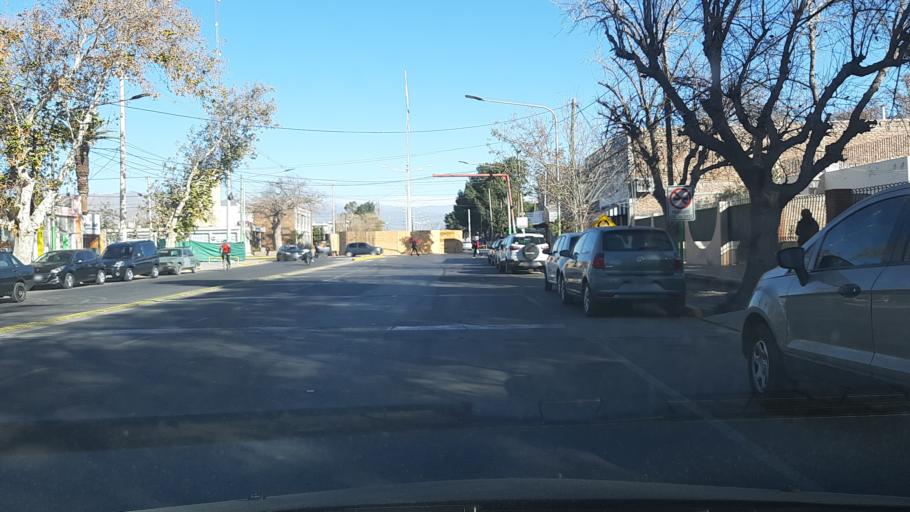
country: AR
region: San Juan
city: San Juan
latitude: -31.5303
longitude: -68.5937
